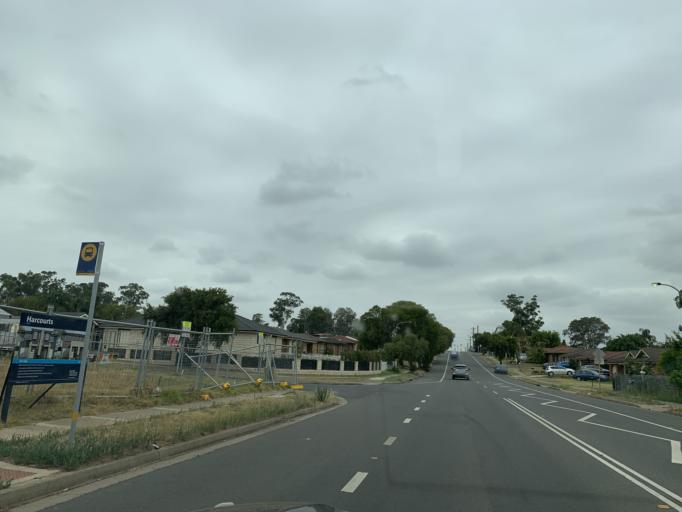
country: AU
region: New South Wales
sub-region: Blacktown
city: Doonside
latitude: -33.7540
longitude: 150.8712
